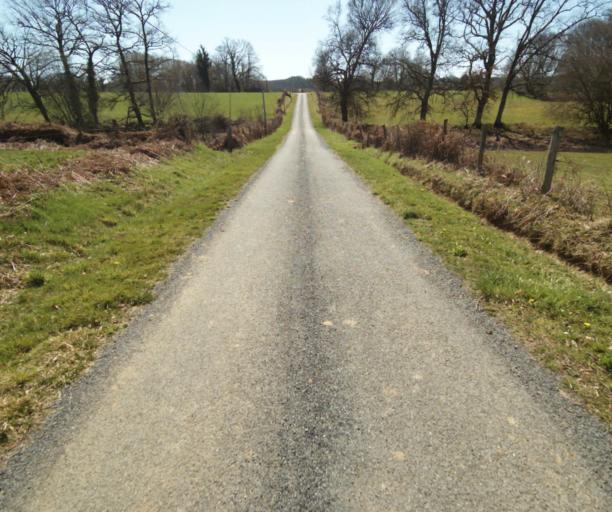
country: FR
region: Limousin
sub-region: Departement de la Correze
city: Uzerche
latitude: 45.3992
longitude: 1.6292
